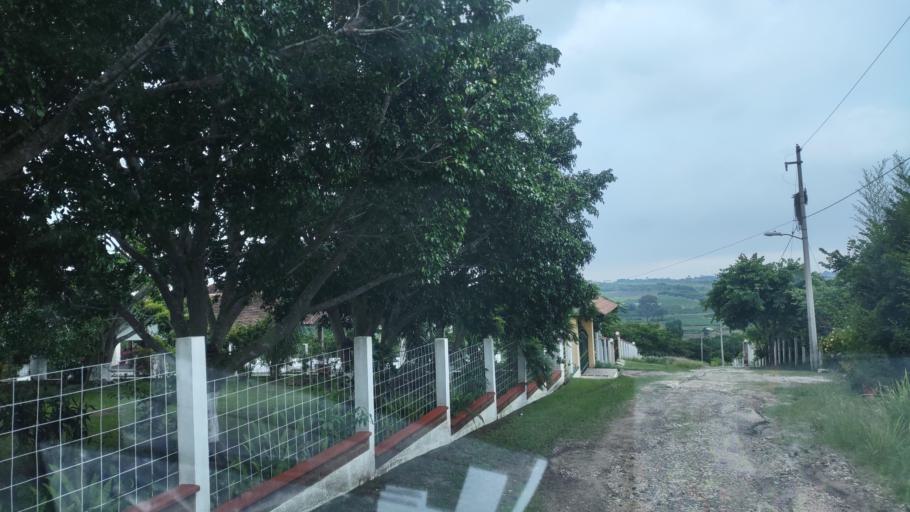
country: MX
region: Veracruz
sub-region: Emiliano Zapata
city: Dos Rios
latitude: 19.4773
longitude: -96.8148
